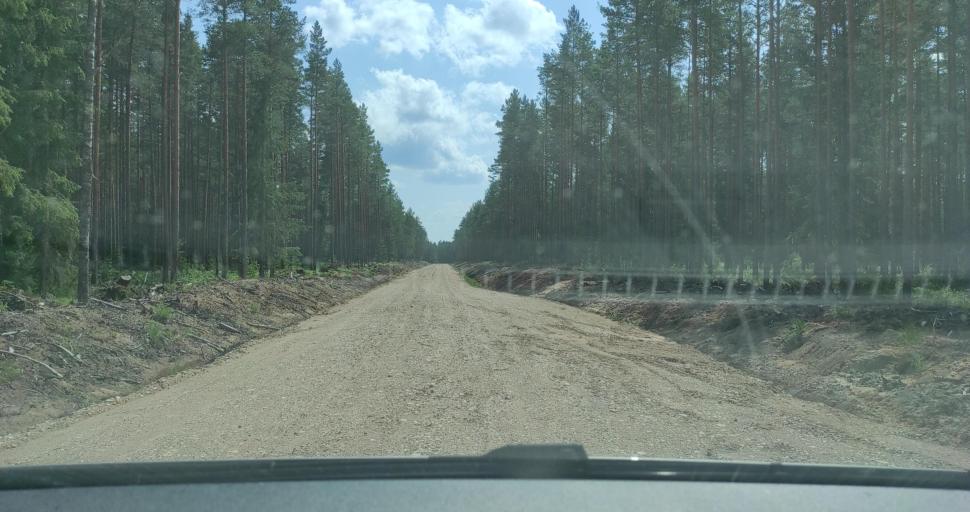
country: LV
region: Kuldigas Rajons
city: Kuldiga
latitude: 57.0578
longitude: 22.1895
